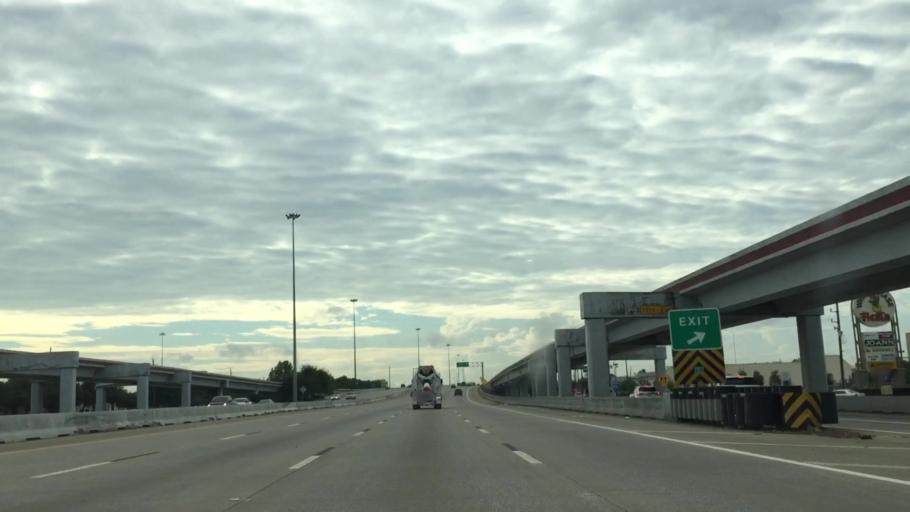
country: US
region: Texas
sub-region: Harris County
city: Jersey Village
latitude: 29.9638
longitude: -95.5515
